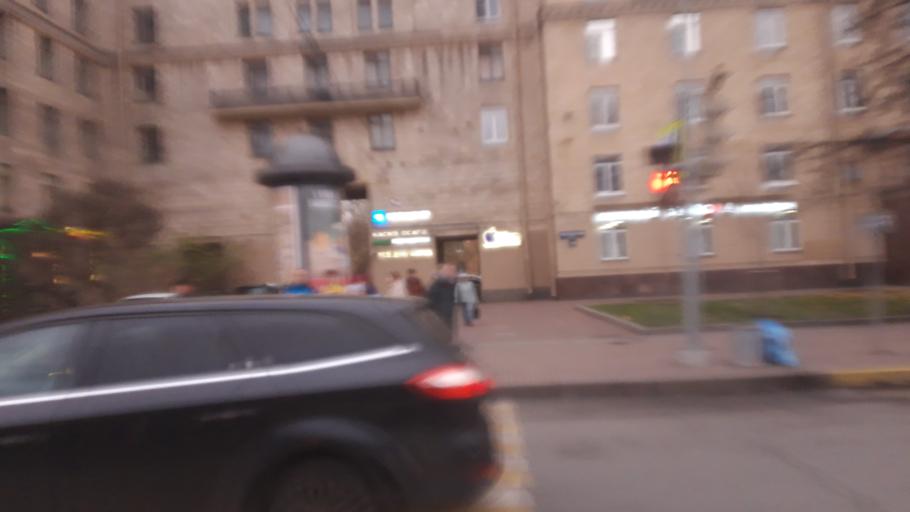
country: RU
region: St.-Petersburg
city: Kupchino
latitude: 59.8508
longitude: 30.3211
